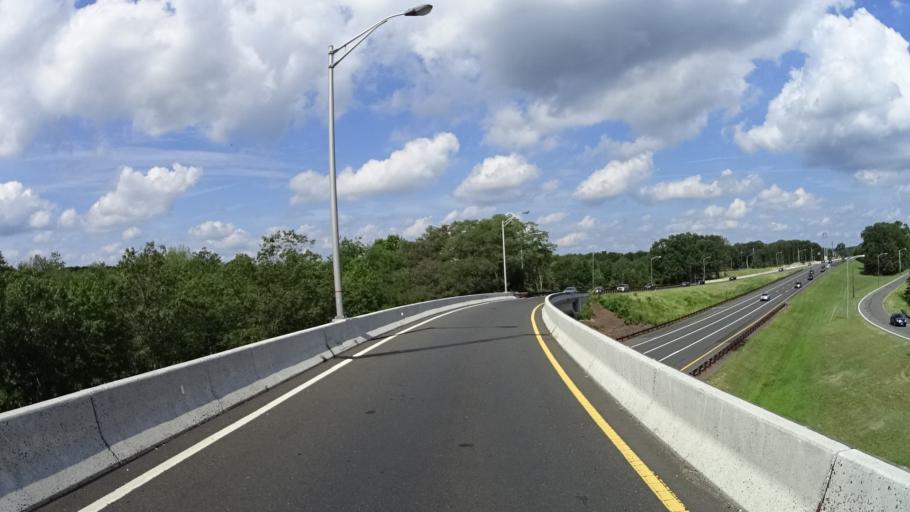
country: US
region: New Jersey
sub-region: Monmouth County
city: Tinton Falls
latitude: 40.2835
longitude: -74.0885
